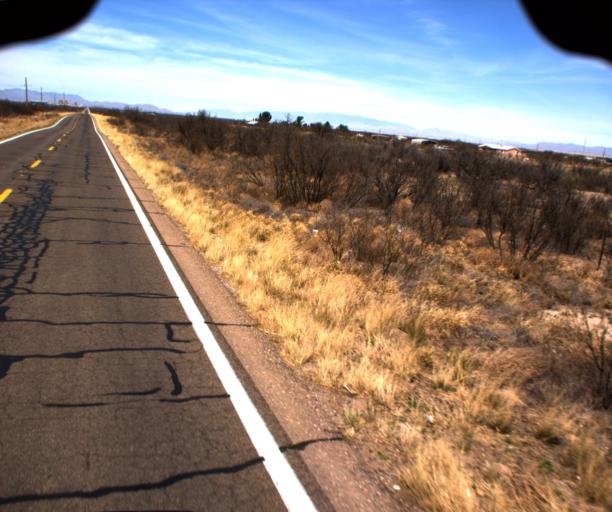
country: US
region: Arizona
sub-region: Cochise County
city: Willcox
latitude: 32.0086
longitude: -109.8652
